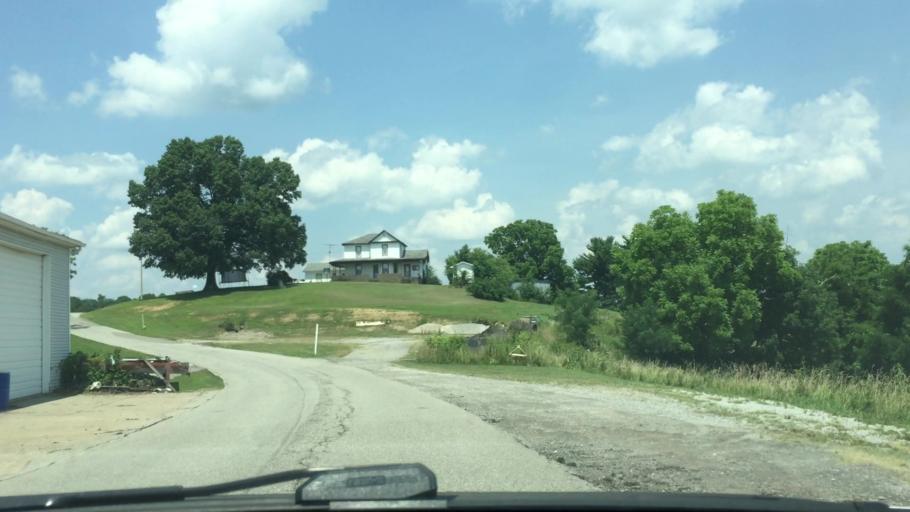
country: US
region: West Virginia
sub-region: Wetzel County
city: New Martinsville
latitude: 39.7057
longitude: -80.7446
